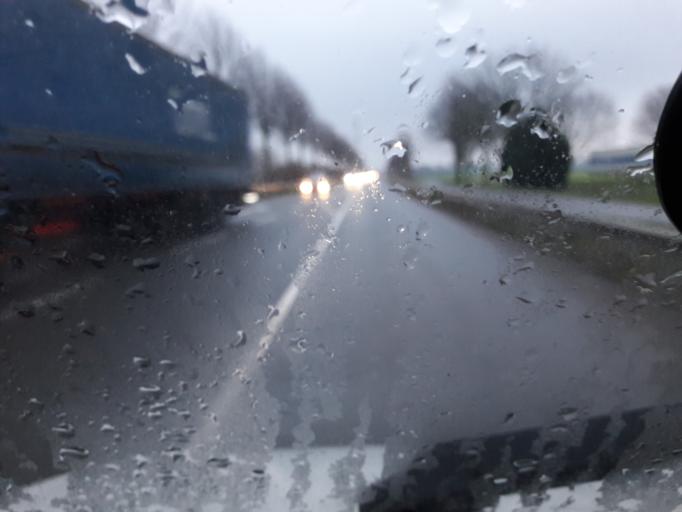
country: DE
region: North Rhine-Westphalia
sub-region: Regierungsbezirk Detmold
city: Hille
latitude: 52.2962
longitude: 8.7766
